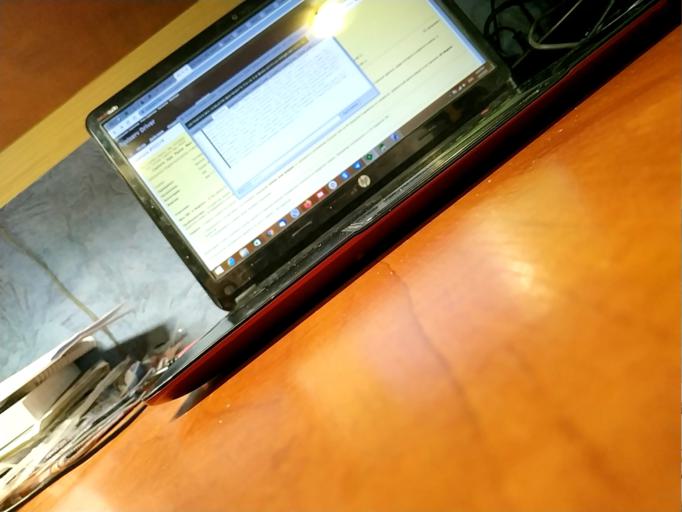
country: RU
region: Tverskaya
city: Sandovo
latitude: 58.4681
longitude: 36.3989
